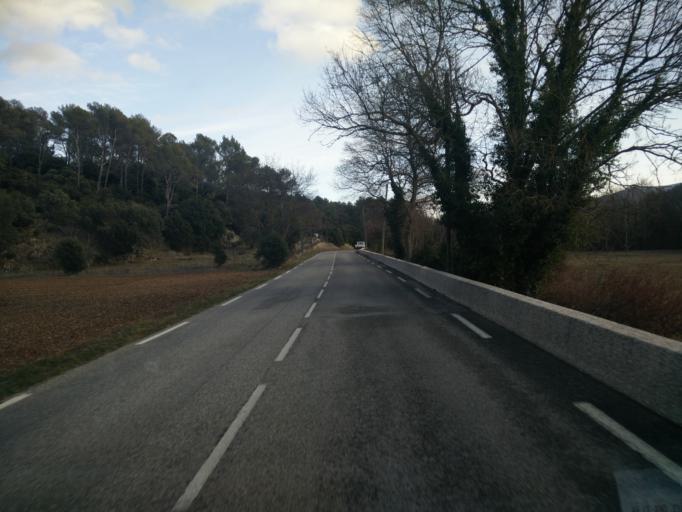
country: FR
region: Provence-Alpes-Cote d'Azur
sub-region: Departement du Var
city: Signes
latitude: 43.2839
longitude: 5.8954
